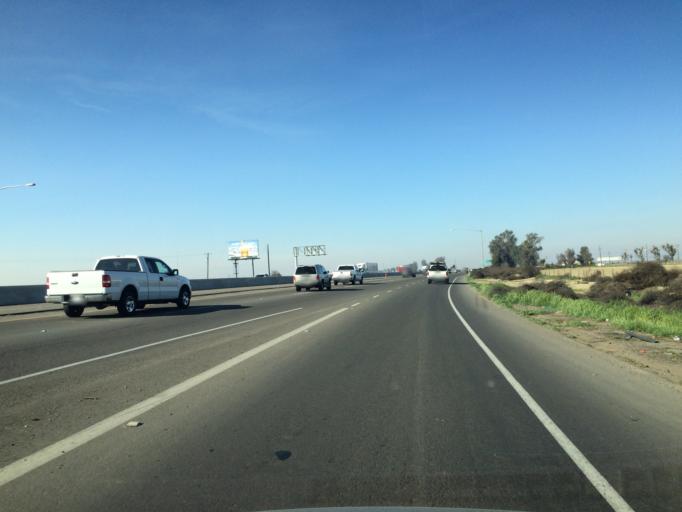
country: US
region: California
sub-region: Tulare County
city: London
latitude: 36.4538
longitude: -119.4911
